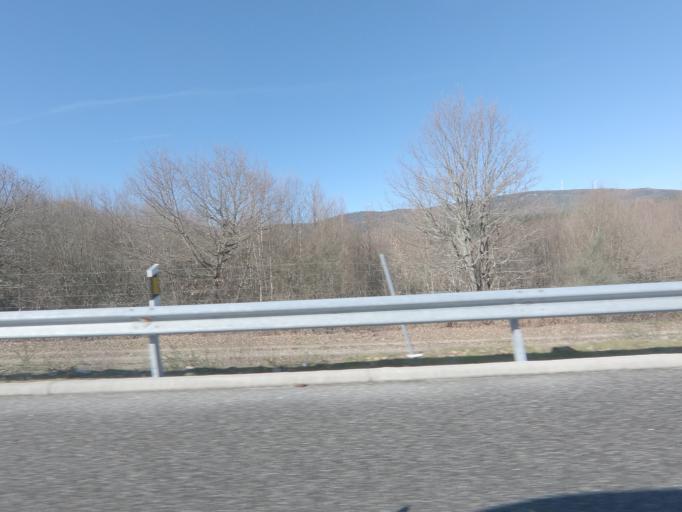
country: ES
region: Galicia
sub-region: Provincia de Ourense
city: Pinor
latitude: 42.4808
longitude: -8.0224
